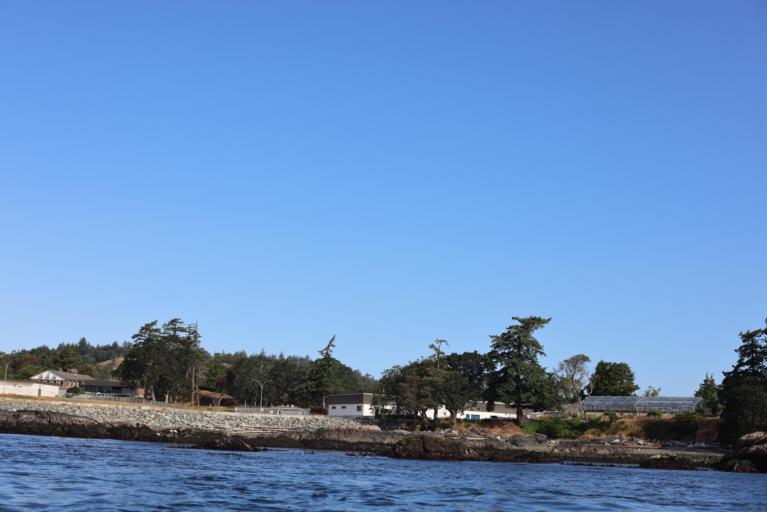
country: CA
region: British Columbia
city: Metchosin
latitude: 48.3382
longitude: -123.5308
